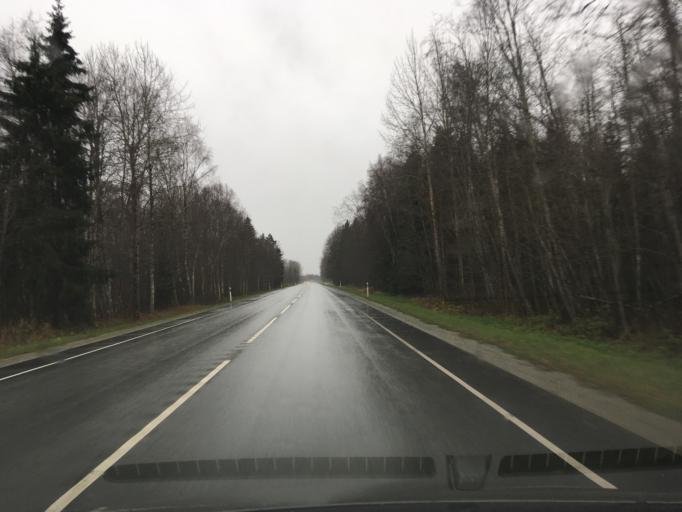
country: EE
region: Harju
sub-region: Nissi vald
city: Riisipere
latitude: 59.1687
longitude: 24.3508
